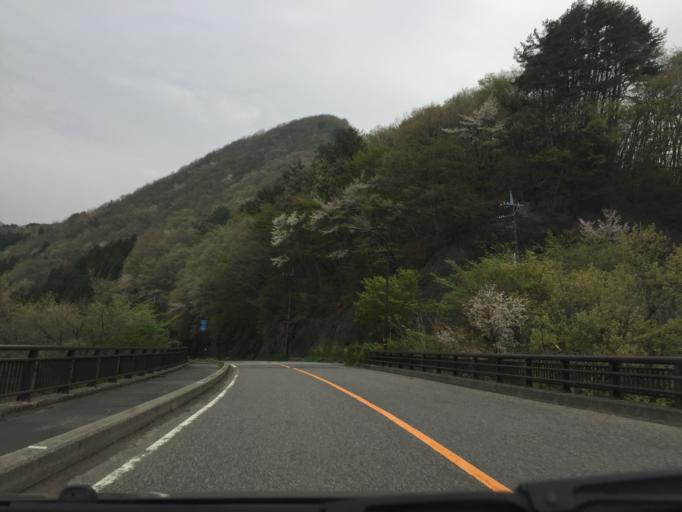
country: JP
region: Tochigi
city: Nikko
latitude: 36.9482
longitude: 139.7003
